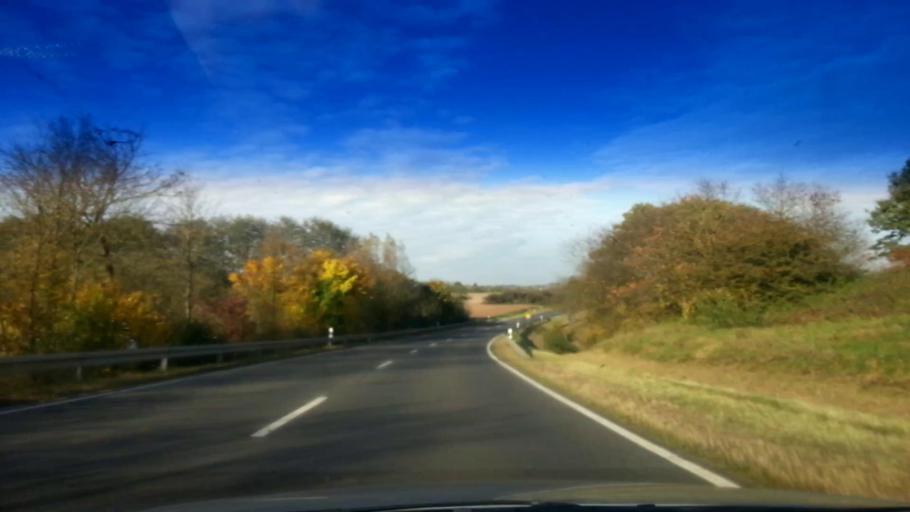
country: DE
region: Bavaria
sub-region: Upper Franconia
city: Stegaurach
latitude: 49.8580
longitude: 10.8792
